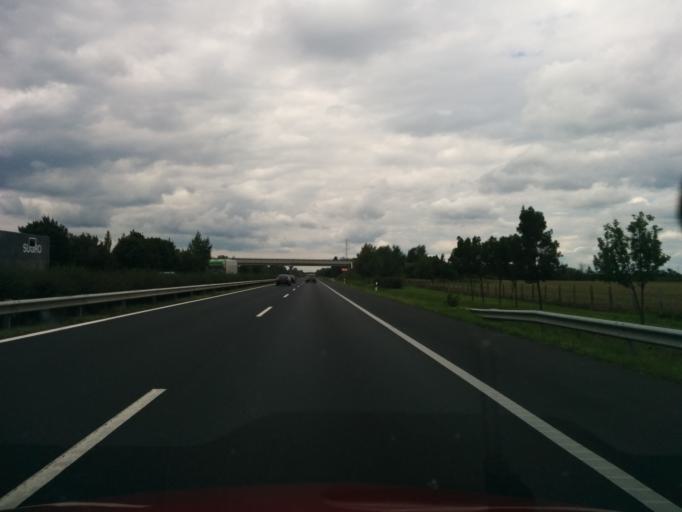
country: HU
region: Gyor-Moson-Sopron
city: Lebeny
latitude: 47.7710
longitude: 17.3732
